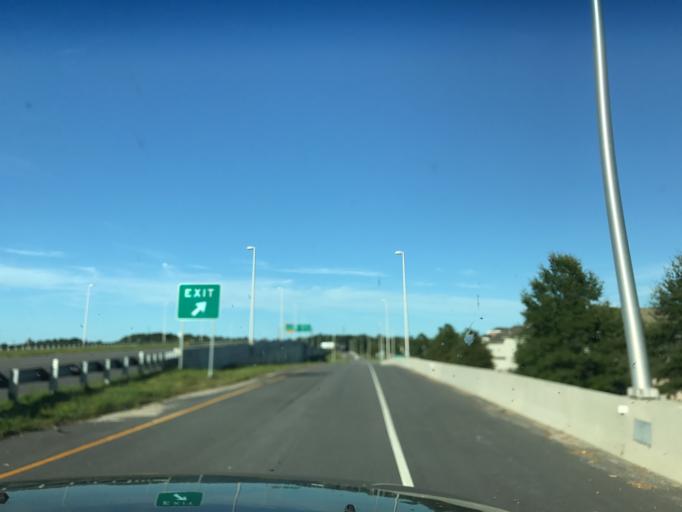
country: US
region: Virginia
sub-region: City of Chesapeake
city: Chesapeake
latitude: 36.7455
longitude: -76.2861
